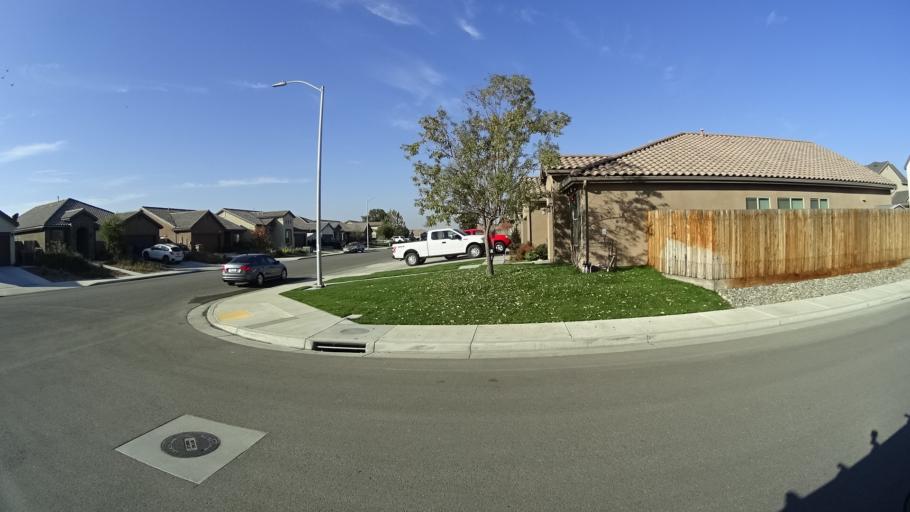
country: US
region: California
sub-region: Kern County
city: Greenfield
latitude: 35.2691
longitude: -119.0713
